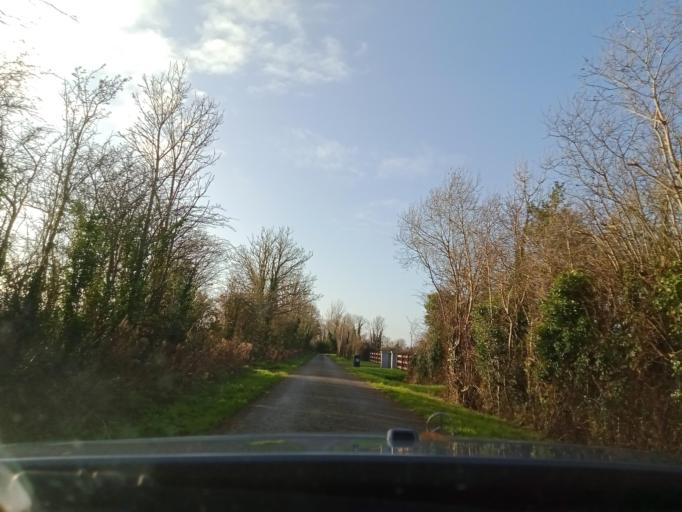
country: IE
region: Leinster
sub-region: Kilkenny
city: Callan
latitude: 52.5232
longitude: -7.3987
